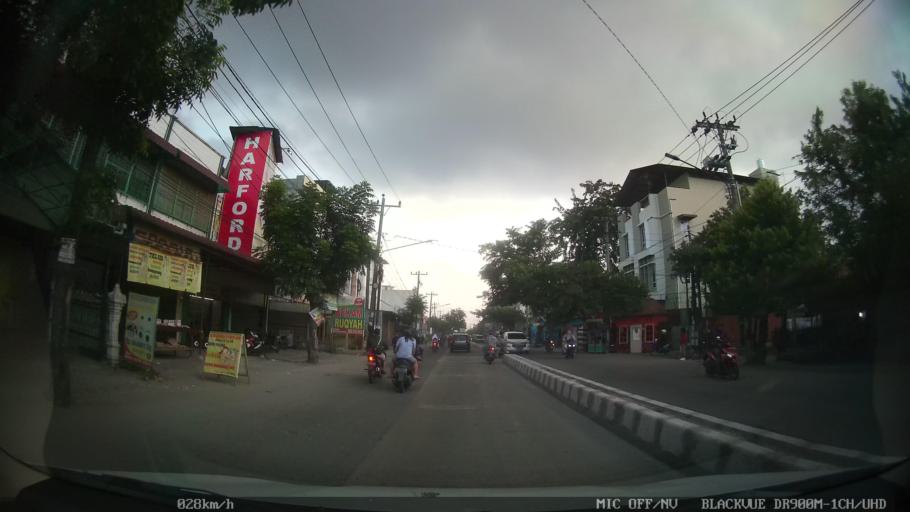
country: ID
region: North Sumatra
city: Medan
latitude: 3.5856
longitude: 98.7113
